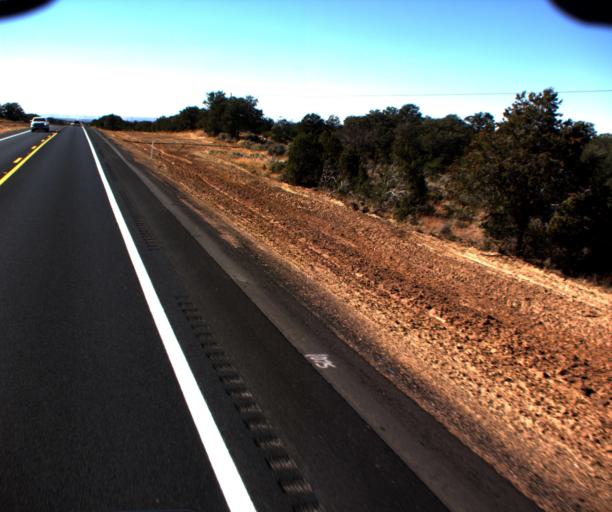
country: US
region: Arizona
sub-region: Apache County
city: Ganado
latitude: 35.7186
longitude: -109.3865
